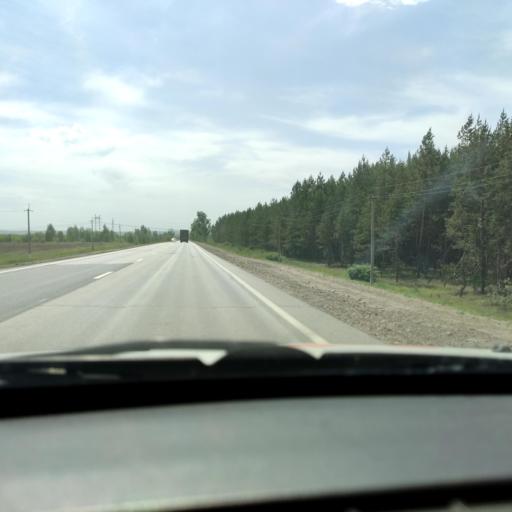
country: RU
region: Samara
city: Mirnyy
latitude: 53.5136
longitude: 50.3085
